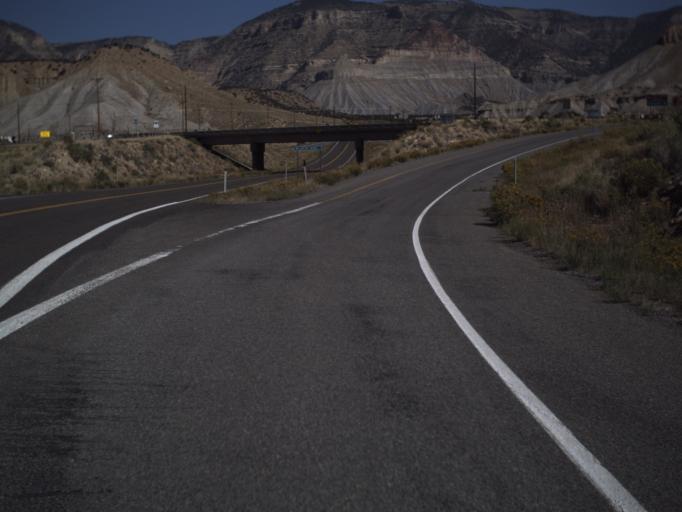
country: US
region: Utah
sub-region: Emery County
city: Orangeville
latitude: 39.2527
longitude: -111.0974
